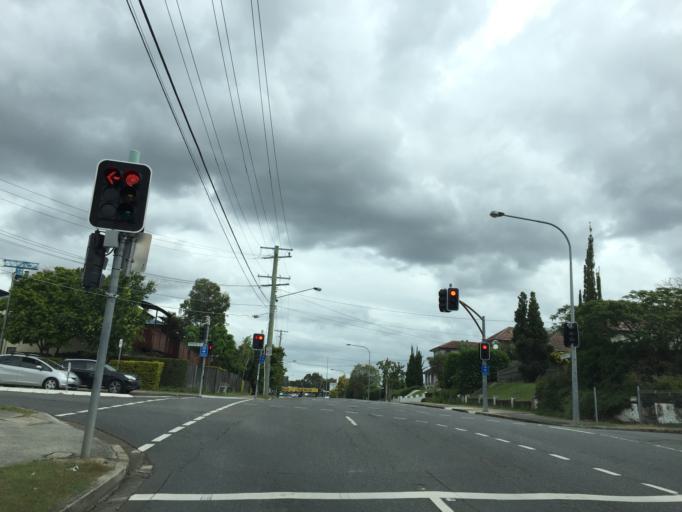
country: AU
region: Queensland
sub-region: Brisbane
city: Wilston
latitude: -27.4361
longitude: 153.0097
